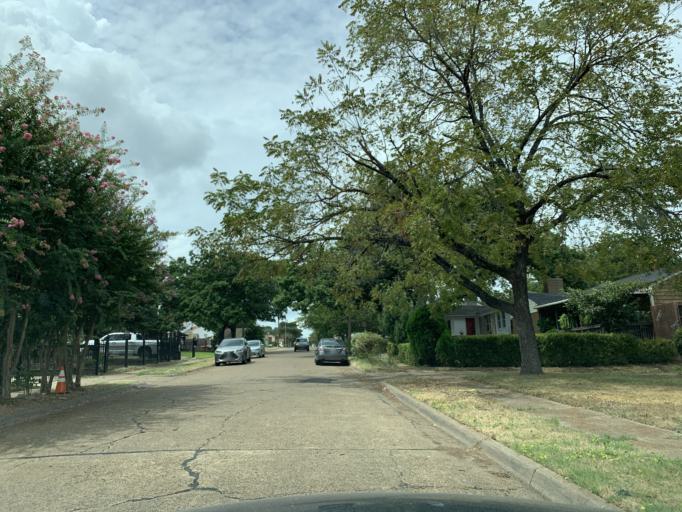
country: US
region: Texas
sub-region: Dallas County
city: Cockrell Hill
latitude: 32.7514
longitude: -96.8651
